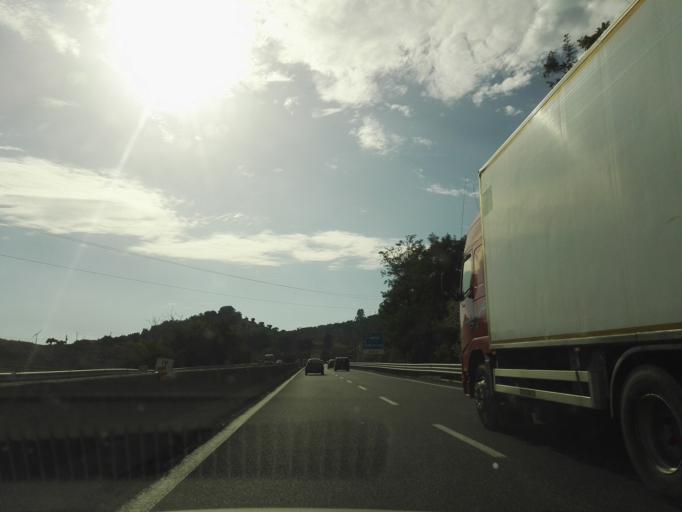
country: IT
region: Calabria
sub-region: Provincia di Catanzaro
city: Marcellinara
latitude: 38.9175
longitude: 16.4869
